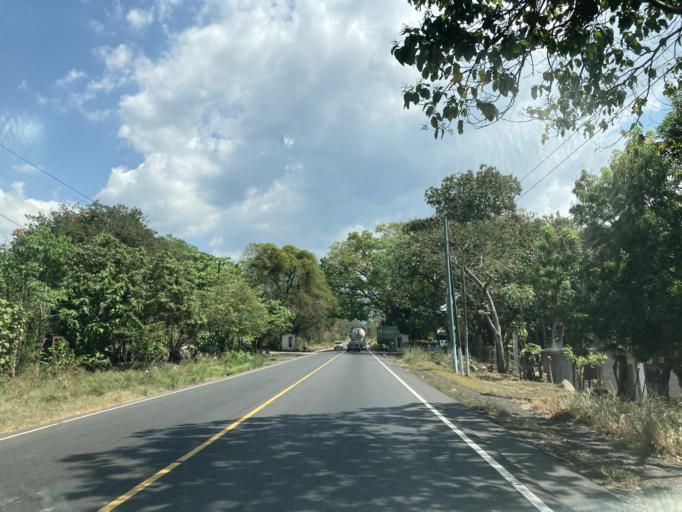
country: GT
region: Santa Rosa
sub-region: Municipio de Taxisco
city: Taxisco
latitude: 14.0955
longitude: -90.5456
